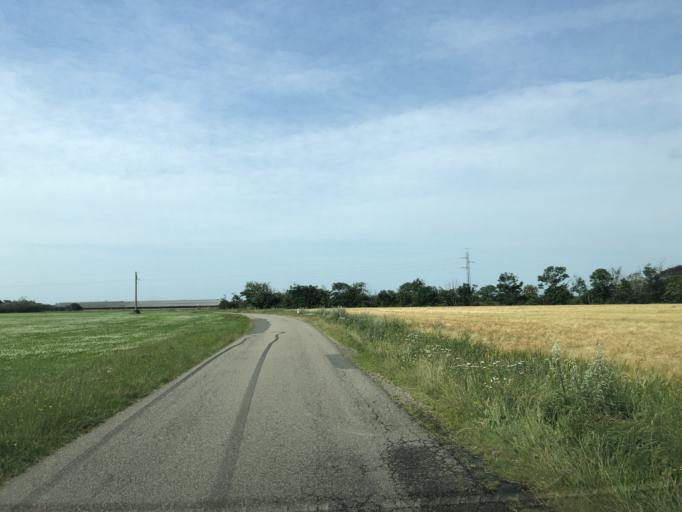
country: DK
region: Central Jutland
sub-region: Lemvig Kommune
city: Lemvig
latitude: 56.4269
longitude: 8.2669
